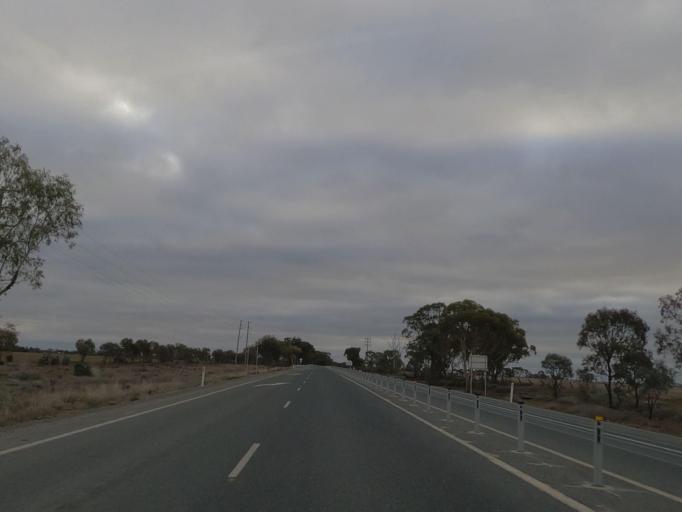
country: AU
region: Victoria
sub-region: Swan Hill
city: Swan Hill
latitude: -35.5500
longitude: 143.7674
